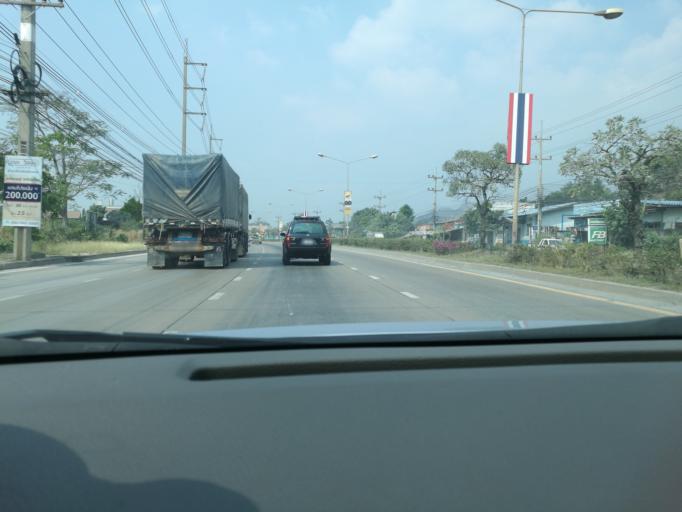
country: TH
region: Sara Buri
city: Phra Phutthabat
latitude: 14.6971
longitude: 100.8651
